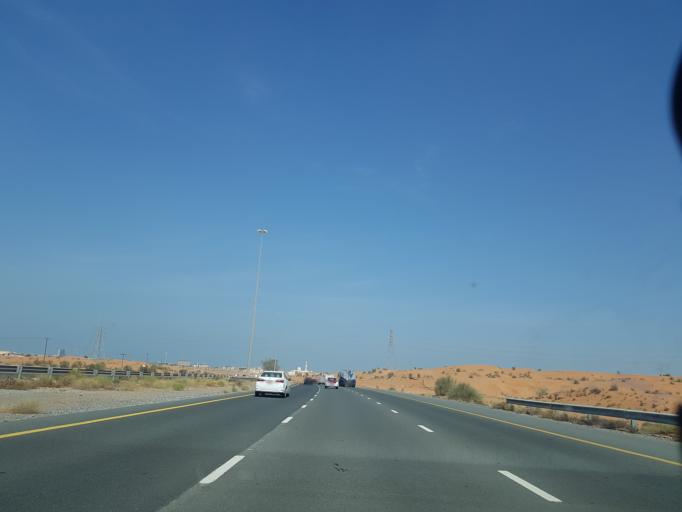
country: AE
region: Ra's al Khaymah
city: Ras al-Khaimah
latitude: 25.6803
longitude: 55.8837
